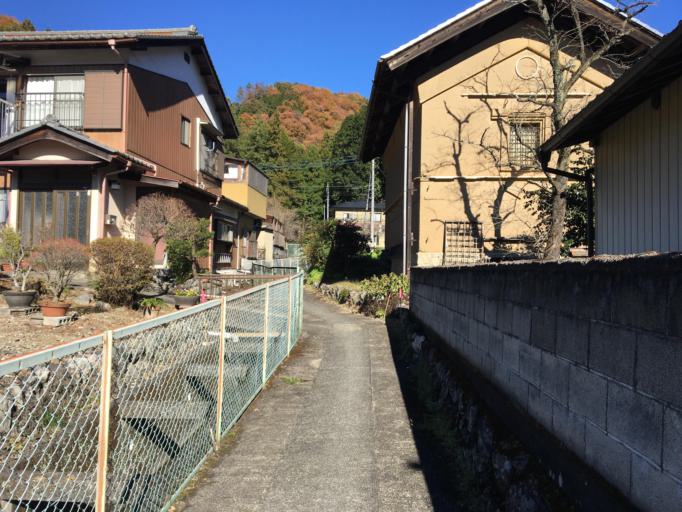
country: JP
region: Saitama
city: Ogawa
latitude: 36.0509
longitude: 139.2112
